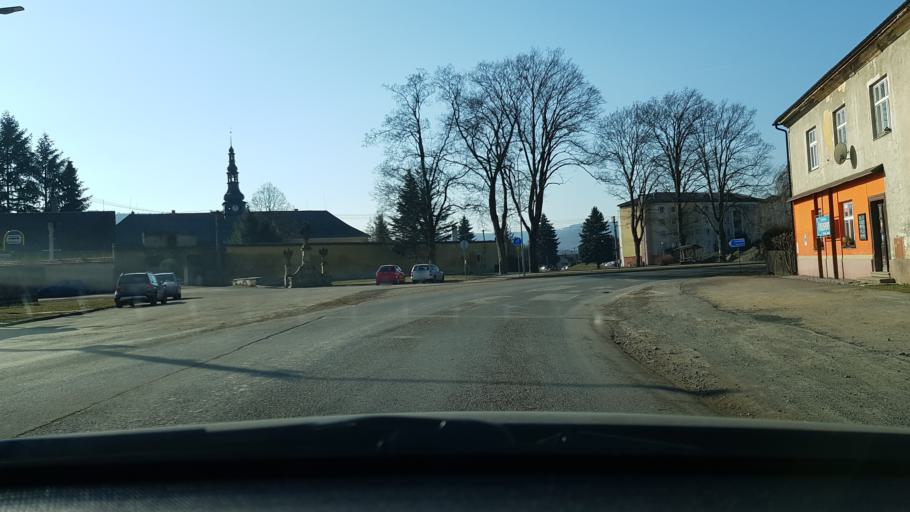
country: CZ
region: Olomoucky
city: Ruda nad Moravou
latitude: 49.9767
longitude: 16.8751
